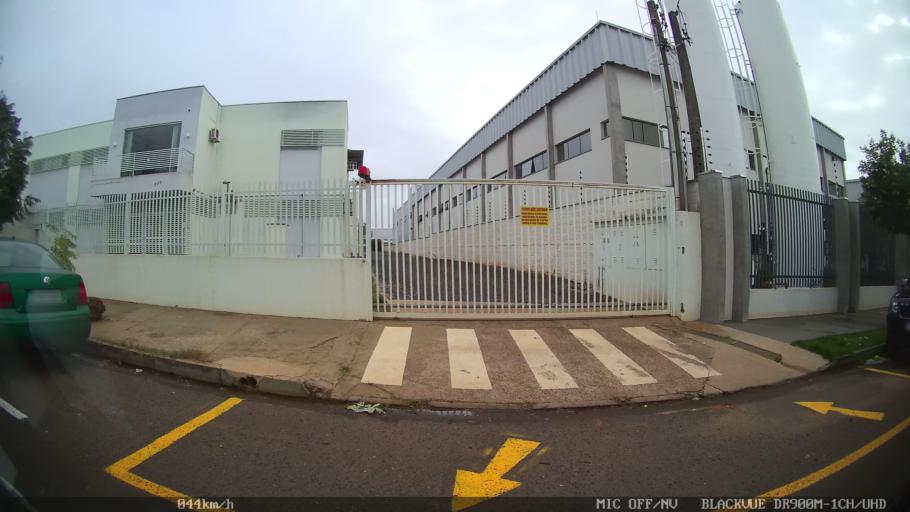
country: BR
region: Sao Paulo
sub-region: Sao Jose Do Rio Preto
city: Sao Jose do Rio Preto
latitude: -20.8287
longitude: -49.4198
